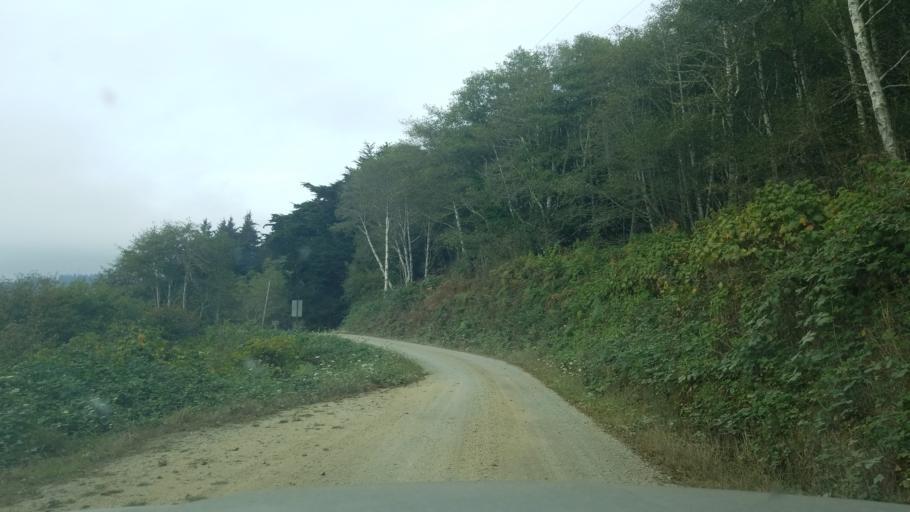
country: US
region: California
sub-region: Del Norte County
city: Bertsch-Oceanview
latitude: 41.5260
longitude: -124.0792
